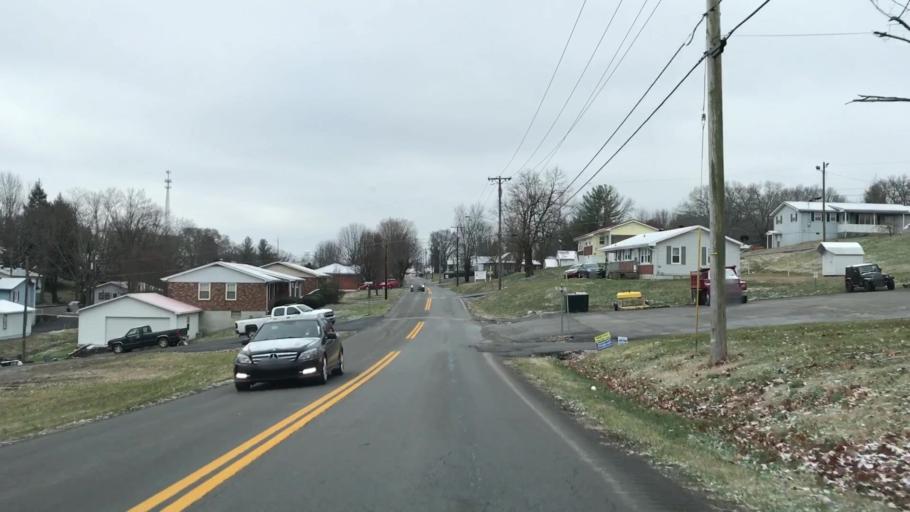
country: US
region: Kentucky
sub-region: Adair County
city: Columbia
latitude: 37.0951
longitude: -85.3088
